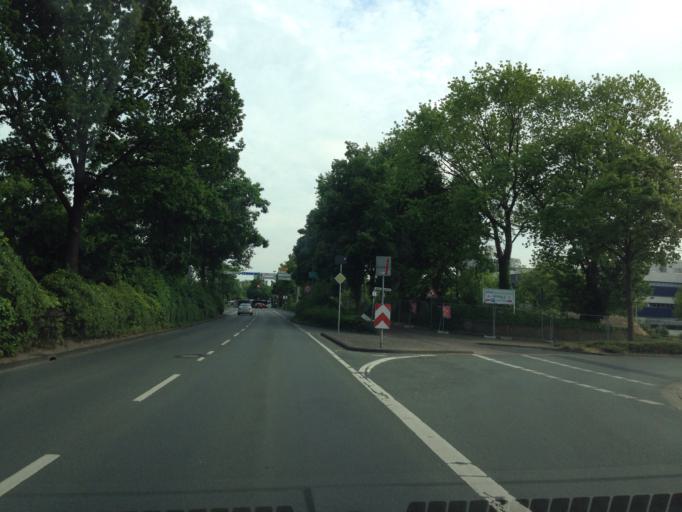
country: DE
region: North Rhine-Westphalia
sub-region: Regierungsbezirk Munster
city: Muenster
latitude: 51.9671
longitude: 7.6018
